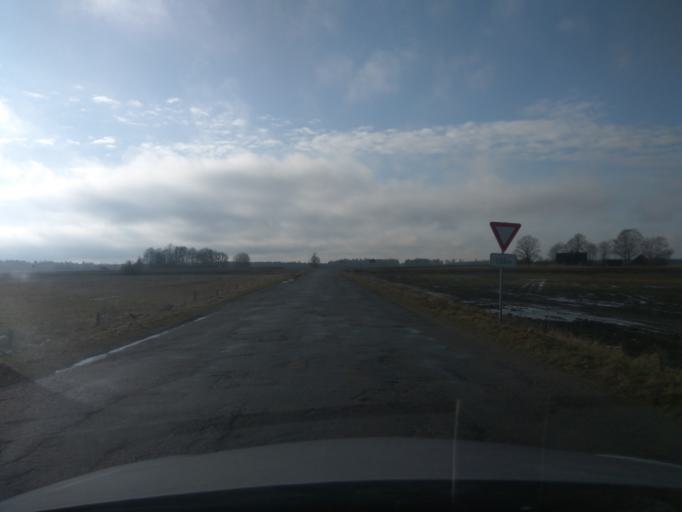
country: LV
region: Saldus Rajons
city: Saldus
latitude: 56.8238
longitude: 22.3794
